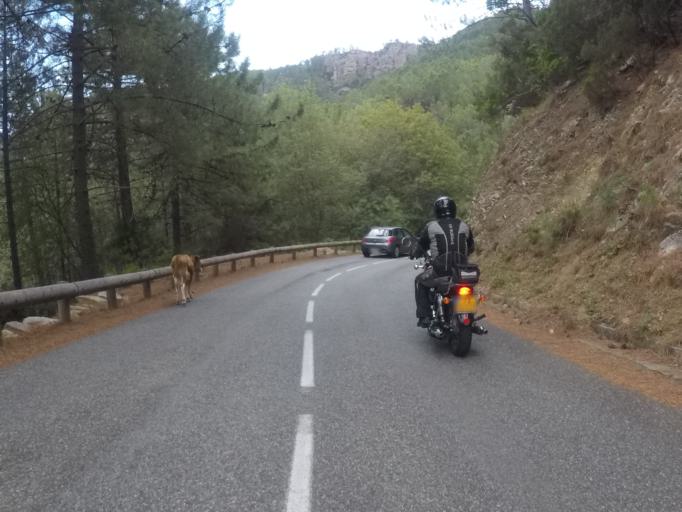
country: FR
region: Corsica
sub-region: Departement de la Corse-du-Sud
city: Sari-Solenzara
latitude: 41.8384
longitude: 9.2881
